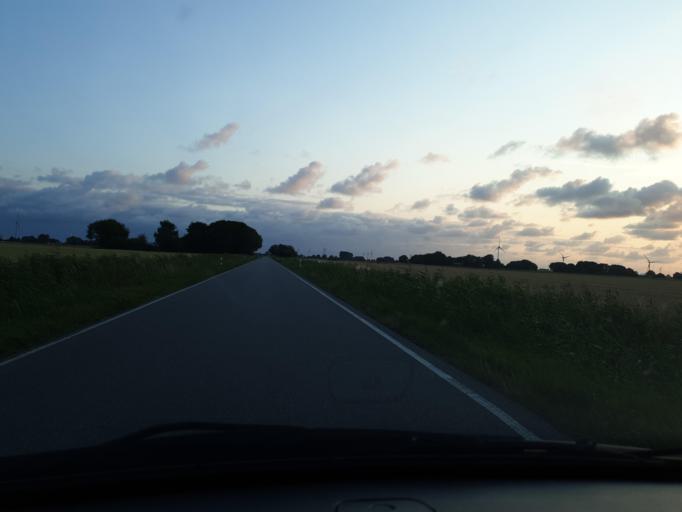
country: DE
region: Schleswig-Holstein
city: Diekhusen-Fahrstedt
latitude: 53.9389
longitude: 9.0062
